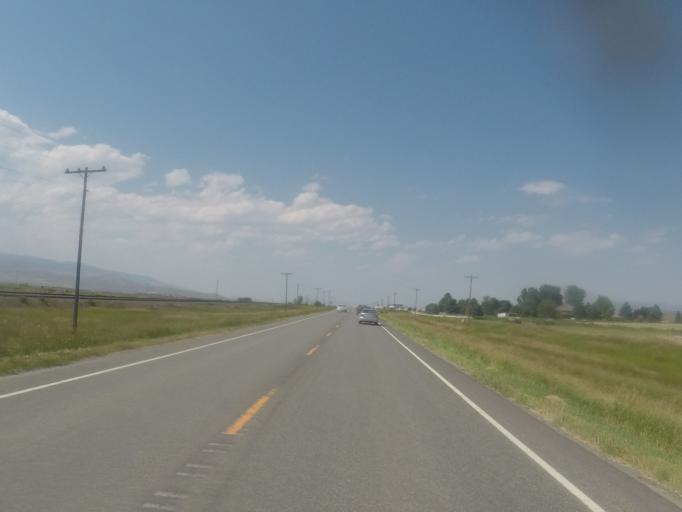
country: US
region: Montana
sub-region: Broadwater County
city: Townsend
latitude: 46.1857
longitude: -111.4466
